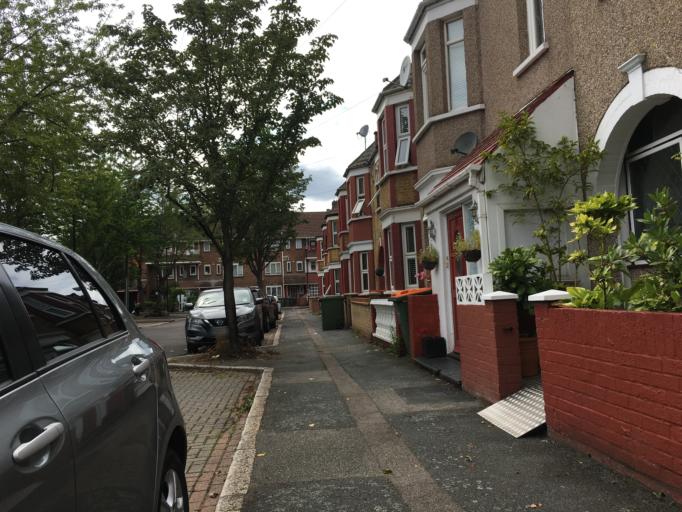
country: GB
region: England
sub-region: Greater London
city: East Ham
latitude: 51.5109
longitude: 0.0215
